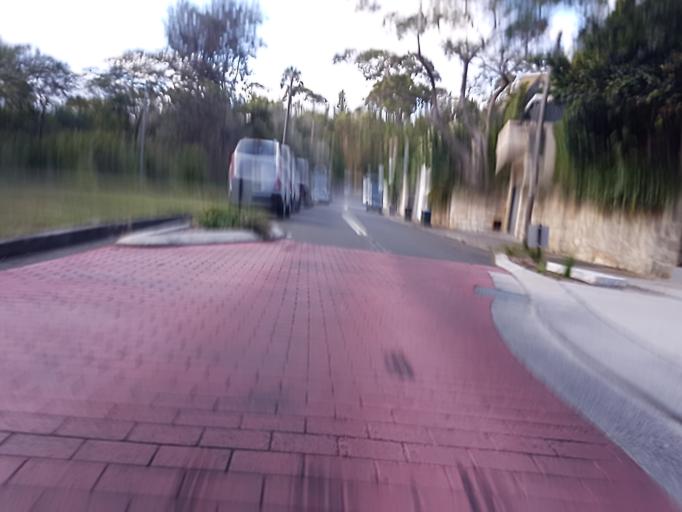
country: AU
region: New South Wales
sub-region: Manly Vale
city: Clontarf
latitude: -33.8181
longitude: 151.2403
